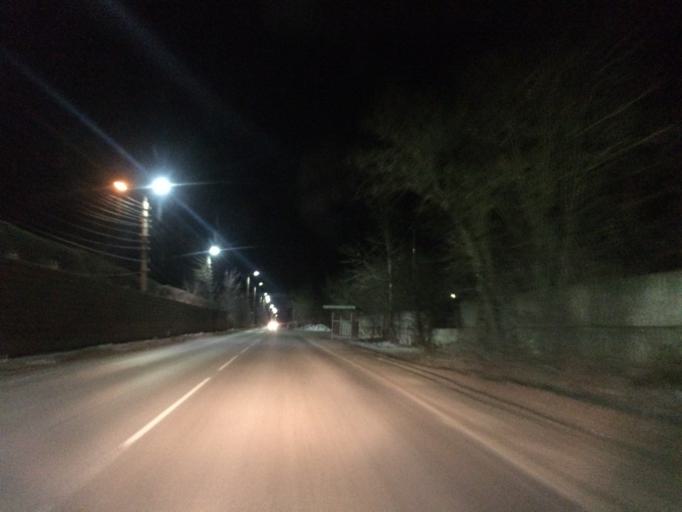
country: RU
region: Tula
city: Mendeleyevskiy
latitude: 54.1441
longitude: 37.5938
